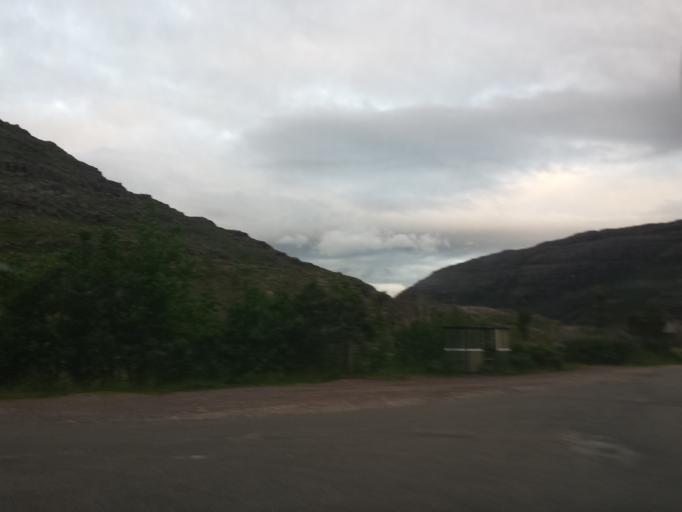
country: GB
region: Scotland
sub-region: Highland
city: Ullapool
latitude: 57.5428
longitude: -5.5011
